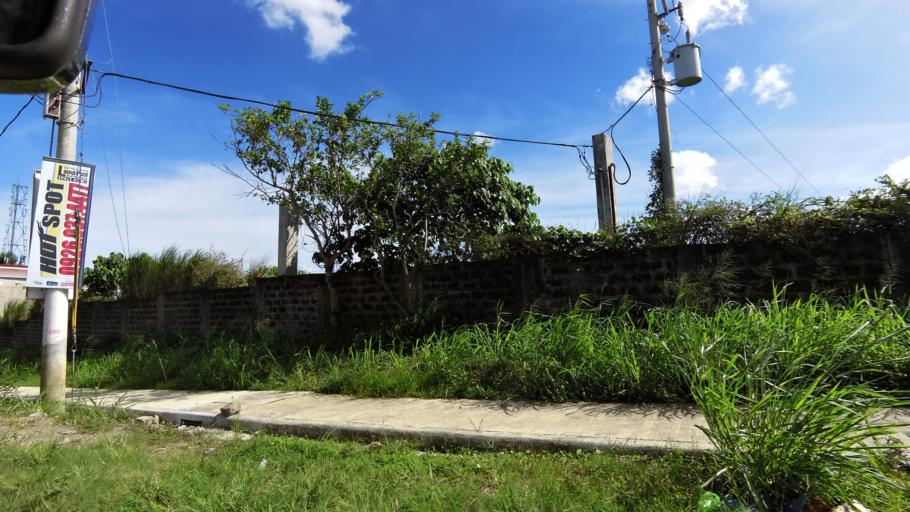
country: PH
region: Calabarzon
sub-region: Province of Cavite
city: Puting Kahoy
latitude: 14.2253
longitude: 121.0433
